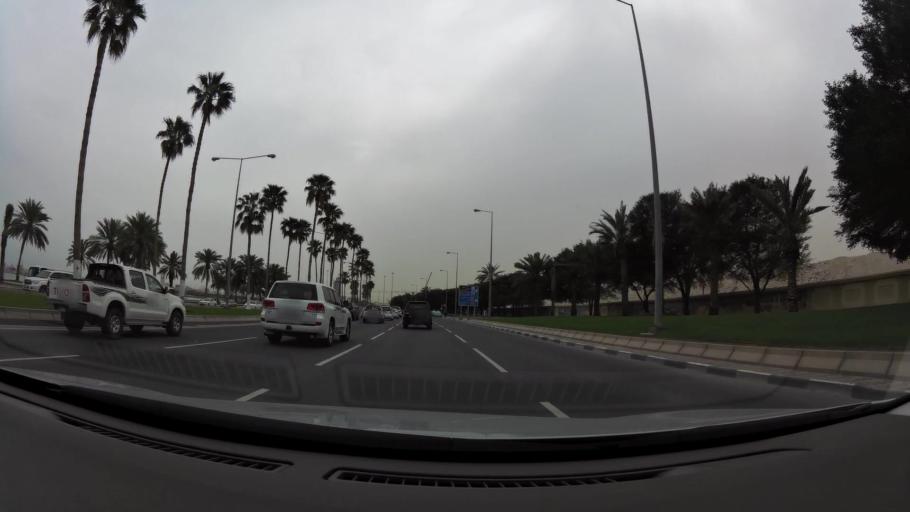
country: QA
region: Baladiyat ad Dawhah
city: Doha
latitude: 25.3075
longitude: 51.5180
